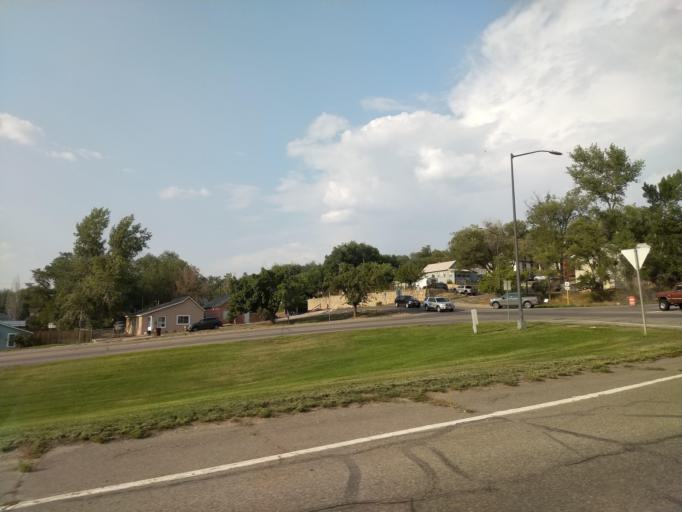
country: US
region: Colorado
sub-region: Garfield County
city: Rifle
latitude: 39.5292
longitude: -107.7813
